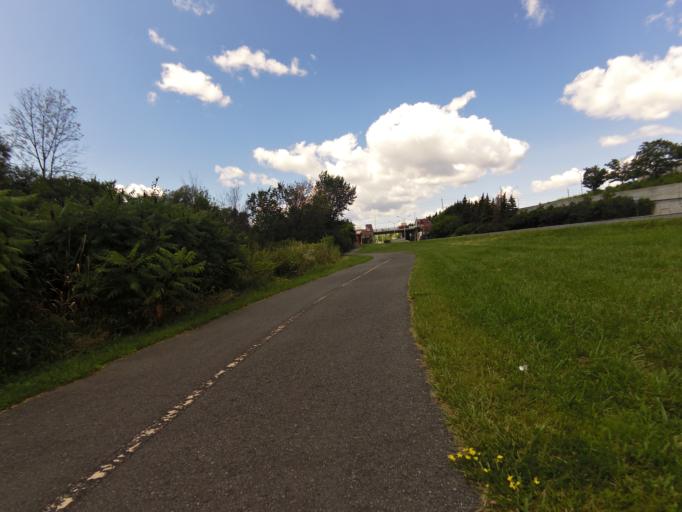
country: CA
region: Ontario
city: Ottawa
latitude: 45.3674
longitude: -75.6659
